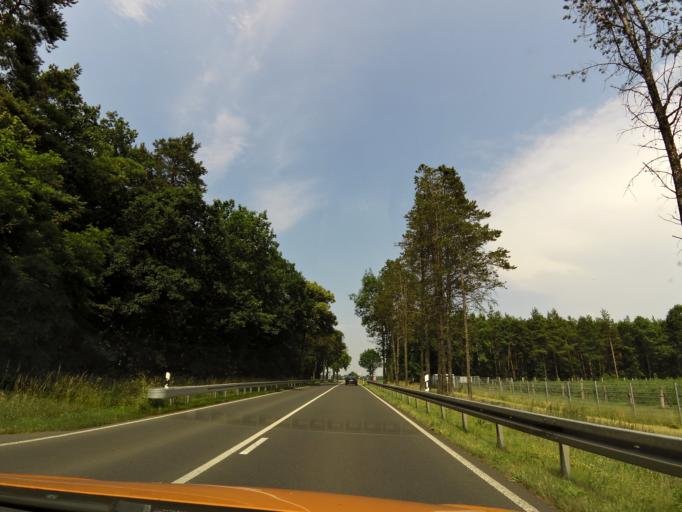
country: DE
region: Brandenburg
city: Pritzwalk
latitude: 53.1780
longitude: 12.1902
